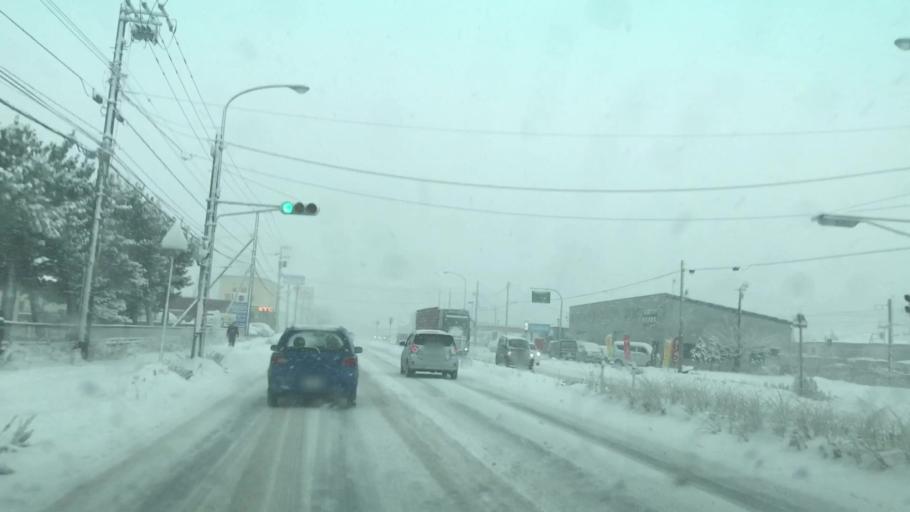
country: JP
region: Hokkaido
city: Muroran
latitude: 42.3845
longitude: 141.0771
